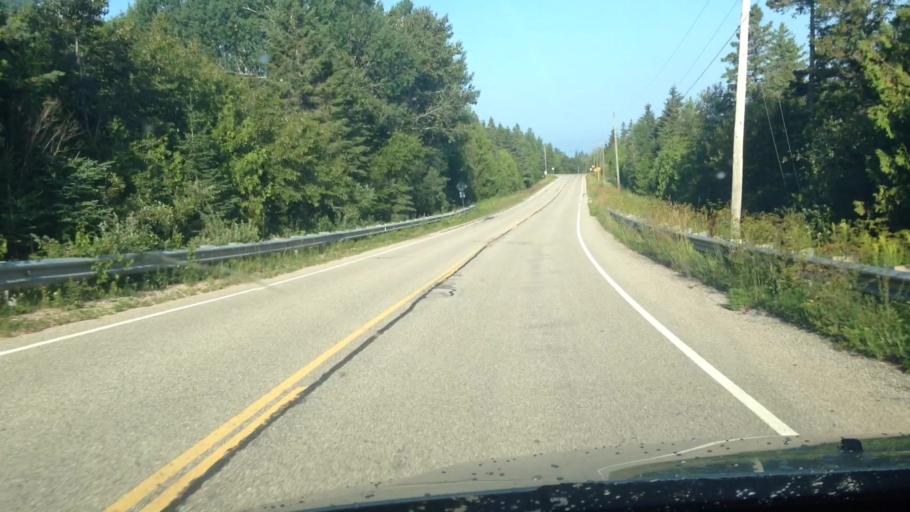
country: US
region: Michigan
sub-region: Mackinac County
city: Saint Ignace
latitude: 45.8921
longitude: -84.8280
